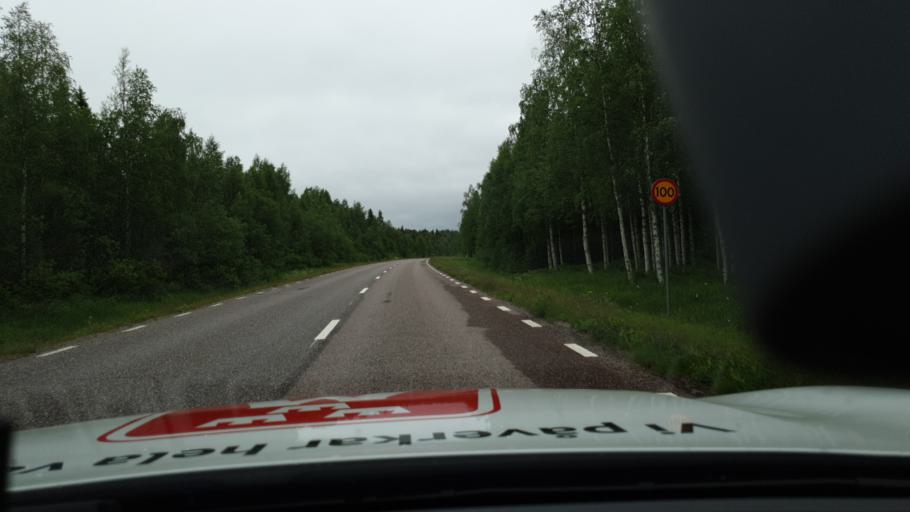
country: FI
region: Lapland
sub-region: Tunturi-Lappi
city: Kolari
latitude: 67.0694
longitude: 23.6632
